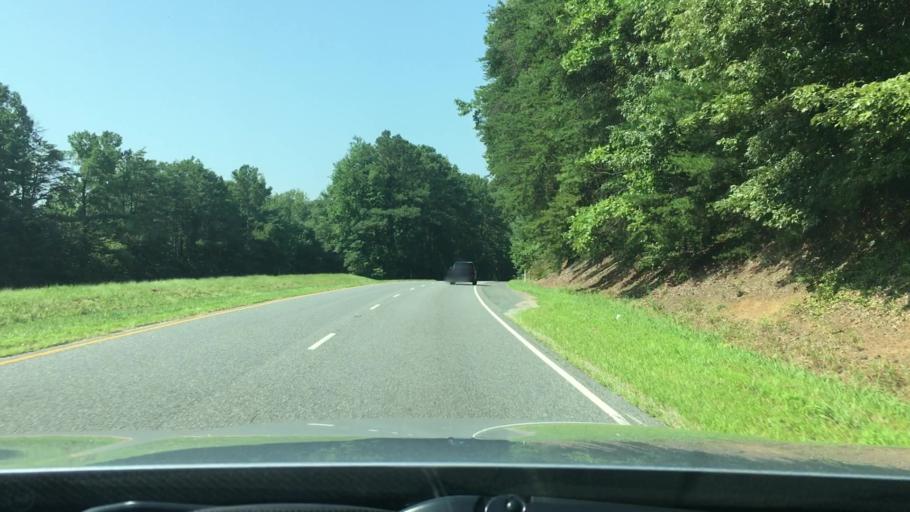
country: US
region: Virginia
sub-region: Caroline County
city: Bowling Green
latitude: 37.9477
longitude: -77.4468
